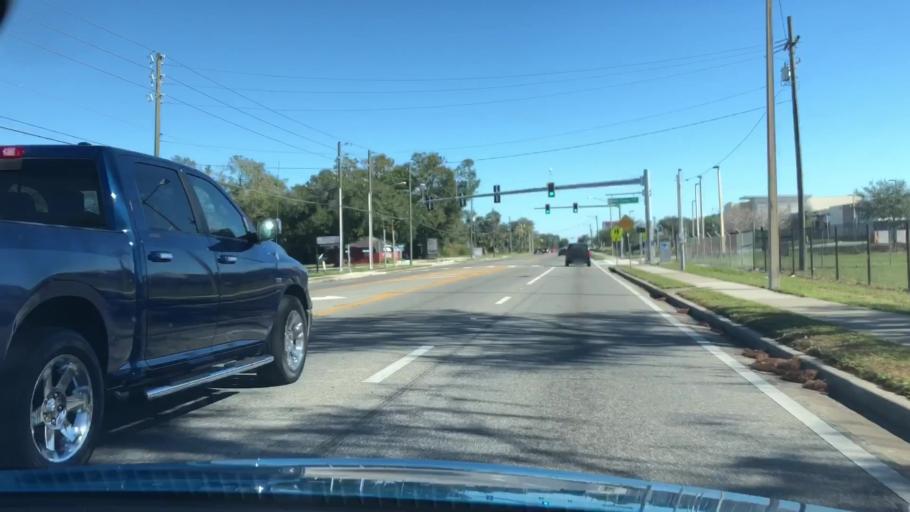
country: US
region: Florida
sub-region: Orange County
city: Sky Lake
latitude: 28.4726
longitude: -81.3881
